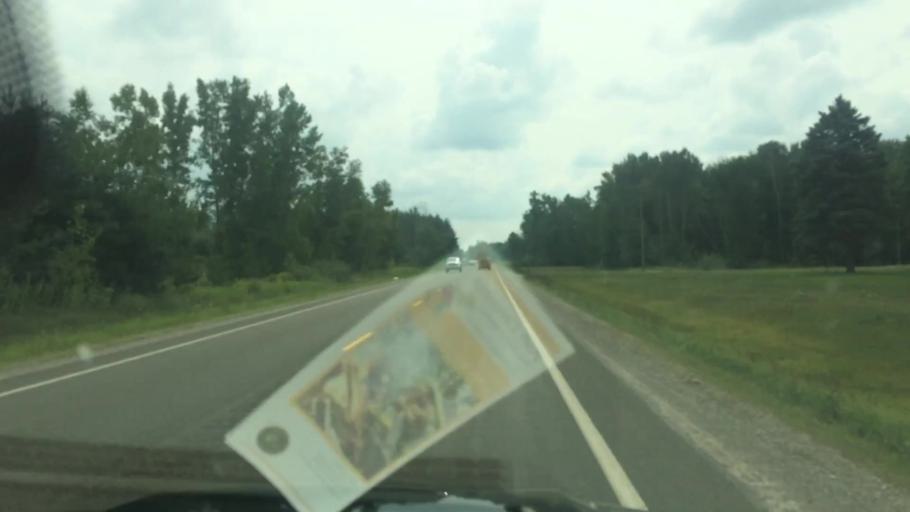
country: US
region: Michigan
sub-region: Tuscola County
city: Cass City
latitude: 43.6528
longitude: -83.0983
